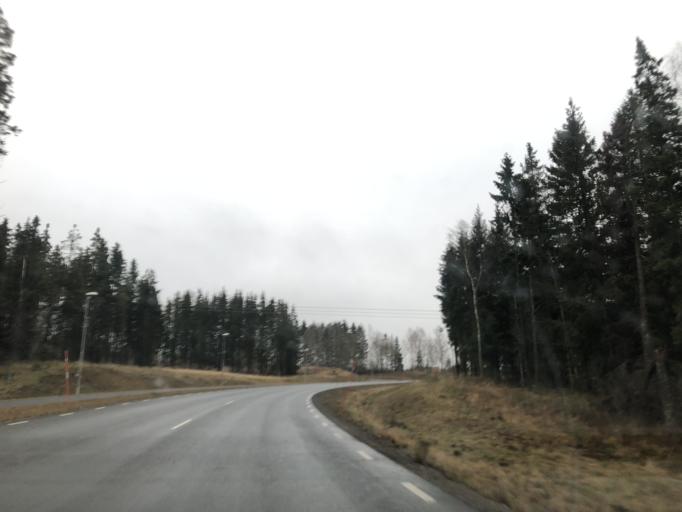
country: SE
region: Vaestra Goetaland
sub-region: Ulricehamns Kommun
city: Ulricehamn
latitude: 57.8161
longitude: 13.2885
